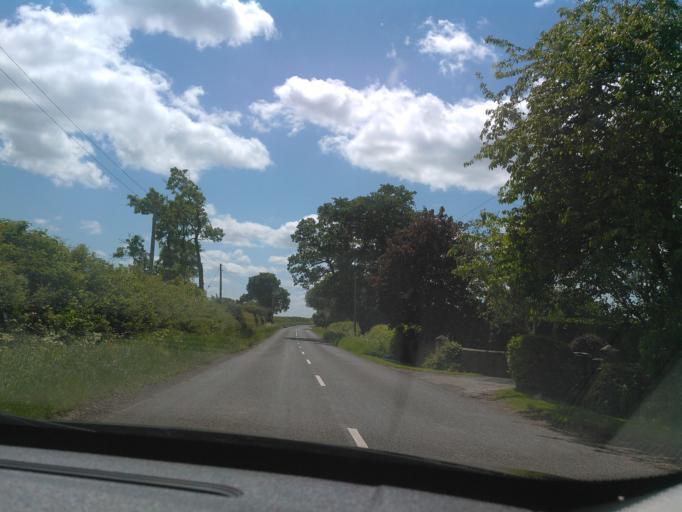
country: GB
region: England
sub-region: Shropshire
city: Wem
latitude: 52.8788
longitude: -2.7154
